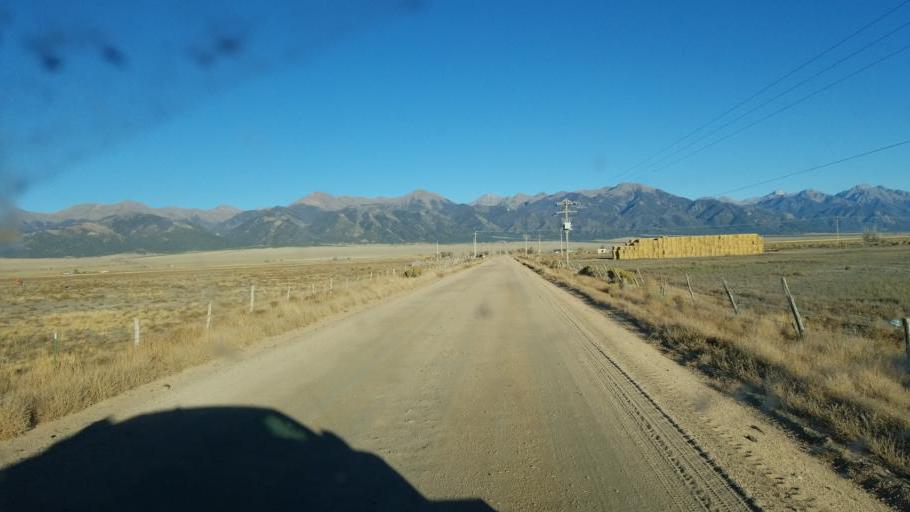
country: US
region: Colorado
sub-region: Saguache County
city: Saguache
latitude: 38.1003
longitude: -105.9062
